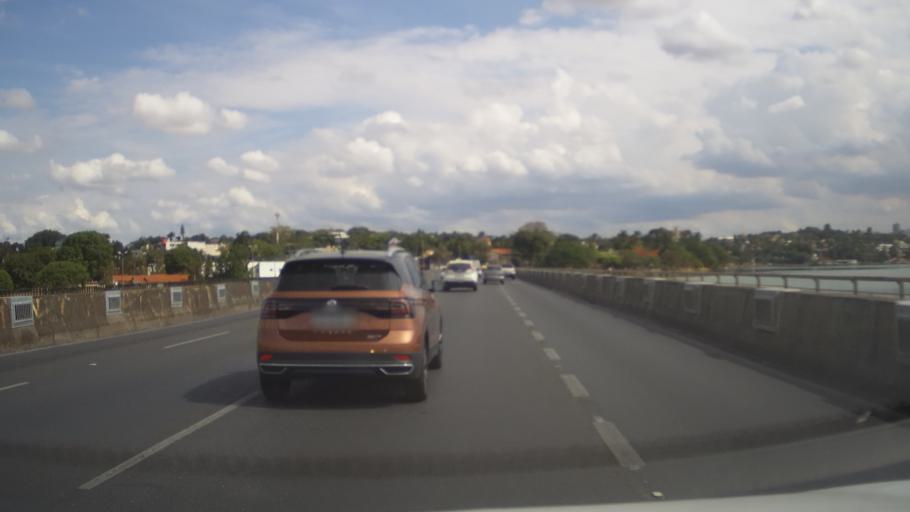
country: BR
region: Minas Gerais
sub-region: Belo Horizonte
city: Belo Horizonte
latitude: -19.8459
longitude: -43.9670
